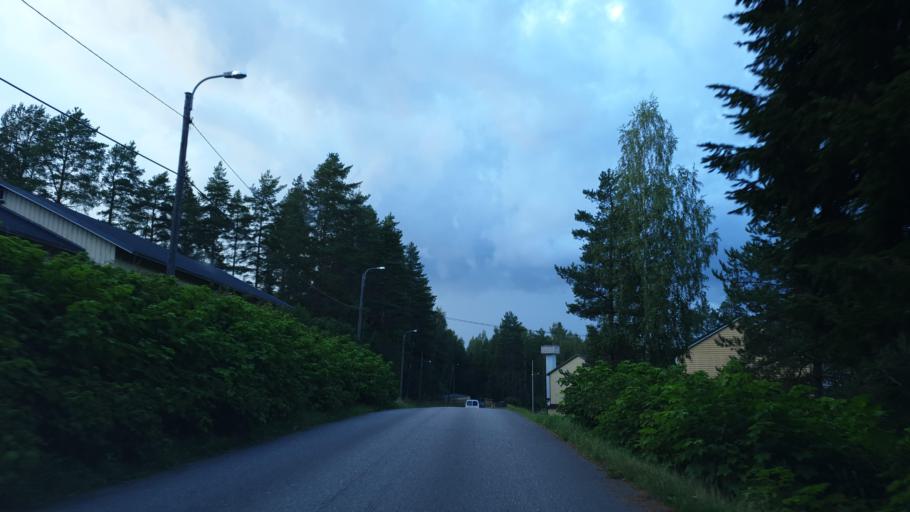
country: FI
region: Northern Savo
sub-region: Varkaus
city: Leppaevirta
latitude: 62.5852
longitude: 27.6077
